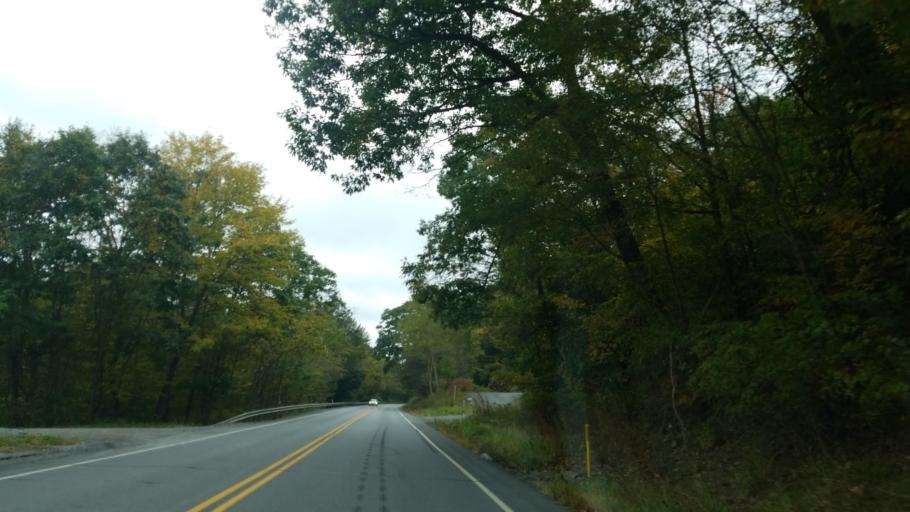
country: US
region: Pennsylvania
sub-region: Clearfield County
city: Curwensville
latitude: 40.9687
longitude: -78.5808
